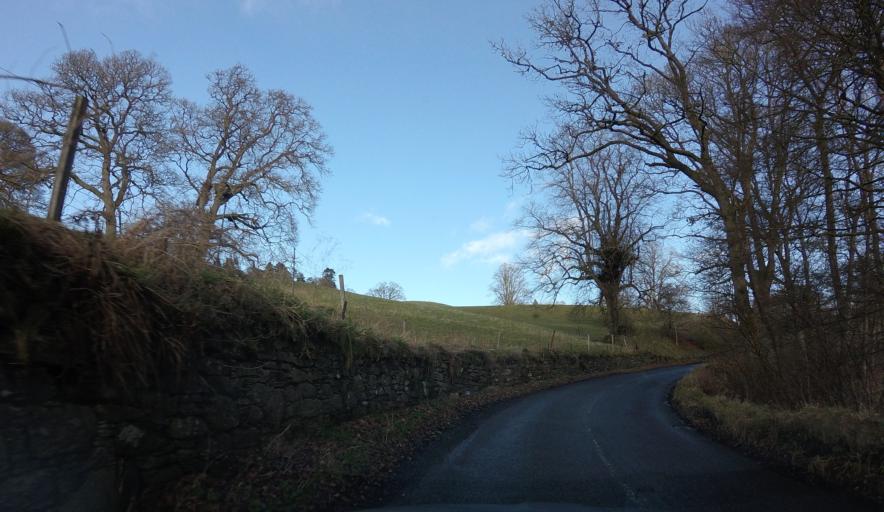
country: GB
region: Scotland
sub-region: Perth and Kinross
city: Pitlochry
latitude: 56.6616
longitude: -3.7614
